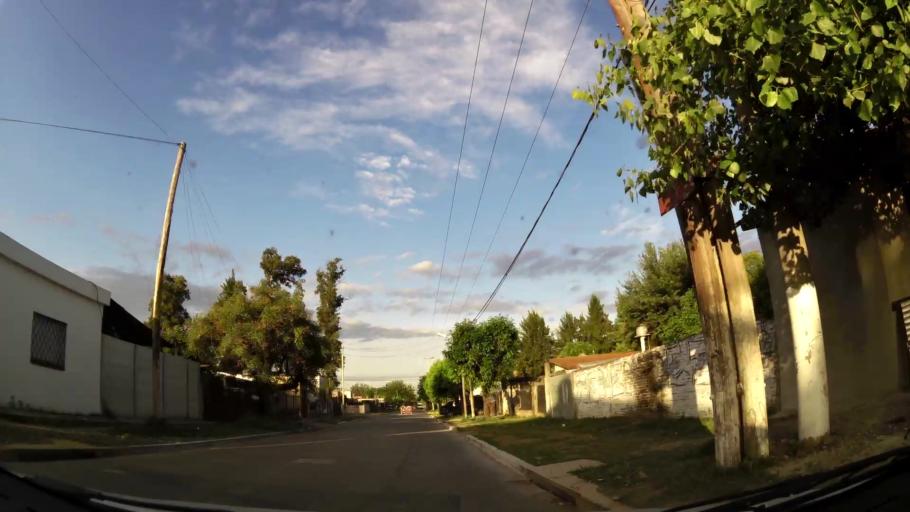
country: AR
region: Buenos Aires
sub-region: Partido de Merlo
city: Merlo
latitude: -34.6800
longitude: -58.7534
